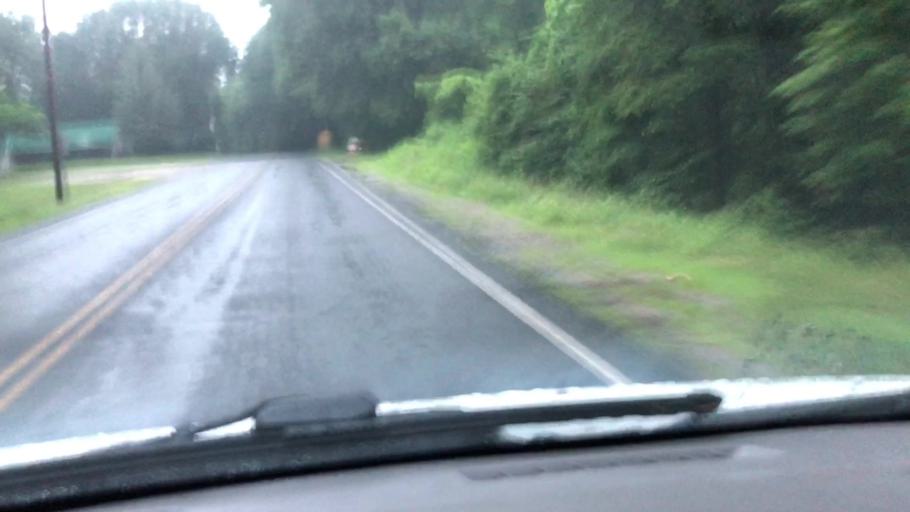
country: US
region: Massachusetts
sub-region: Hampshire County
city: Westhampton
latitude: 42.2767
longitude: -72.7519
